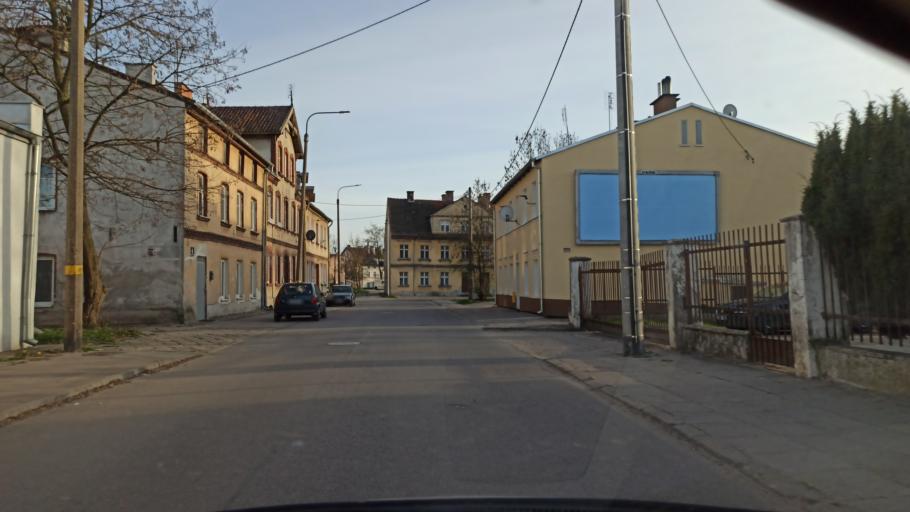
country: PL
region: Warmian-Masurian Voivodeship
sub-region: Powiat elblaski
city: Elblag
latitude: 54.1552
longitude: 19.4039
